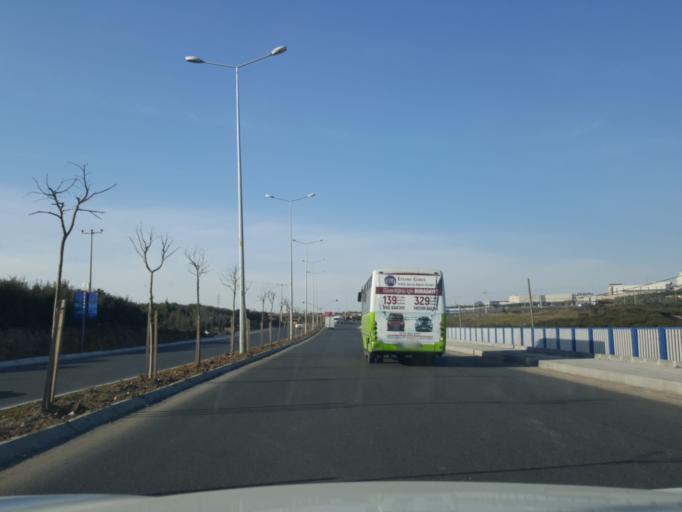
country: TR
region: Kocaeli
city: Tavsancil
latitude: 40.8013
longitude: 29.5519
